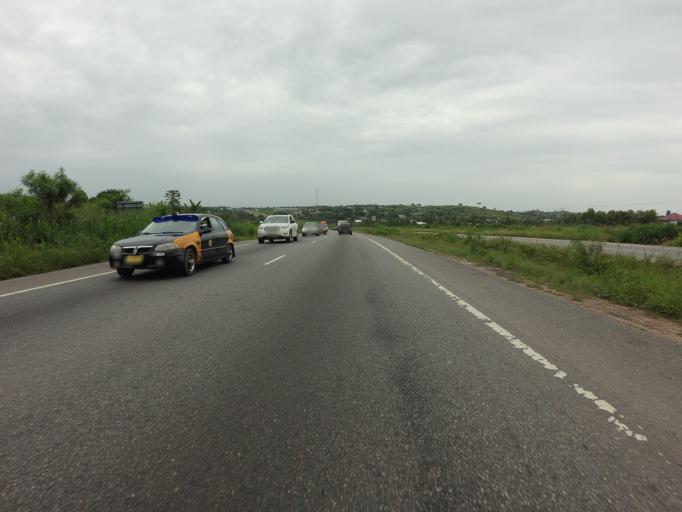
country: GH
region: Eastern
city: Nsawam
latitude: 5.8562
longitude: -0.3588
